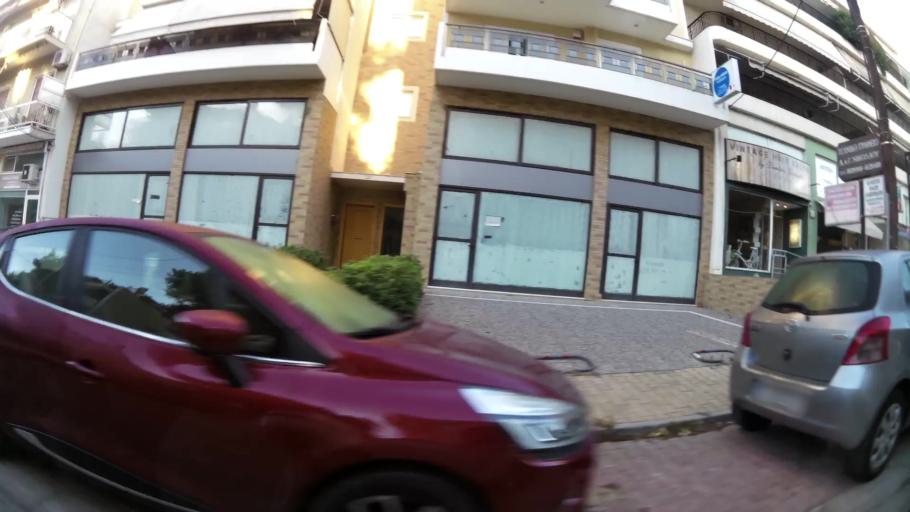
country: GR
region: Attica
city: Pefki
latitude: 38.0553
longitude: 23.7926
